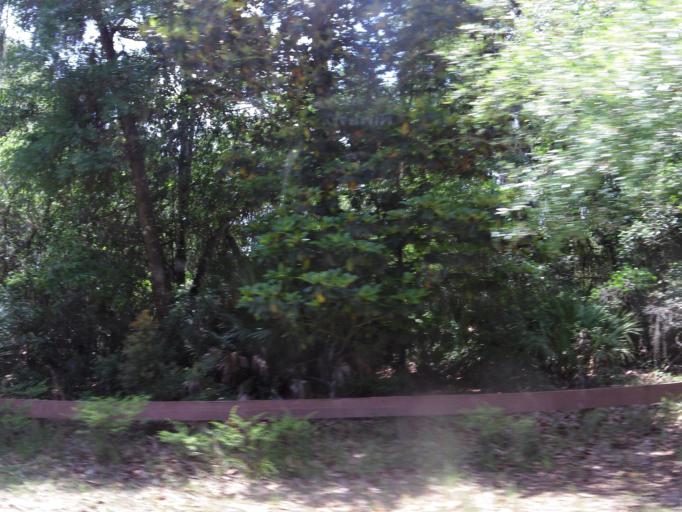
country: US
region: Florida
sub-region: Duval County
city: Atlantic Beach
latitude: 30.4829
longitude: -81.4895
